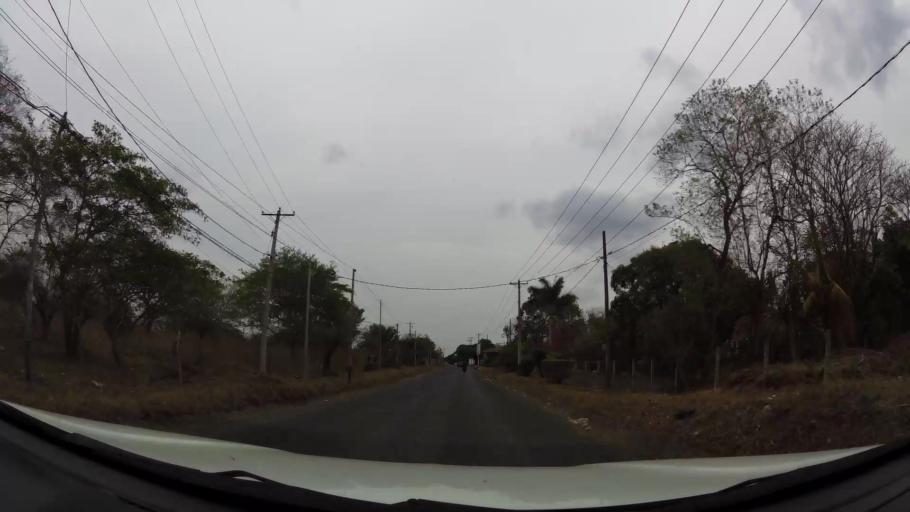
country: NI
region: Masaya
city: Ticuantepe
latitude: 12.0669
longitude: -86.1864
